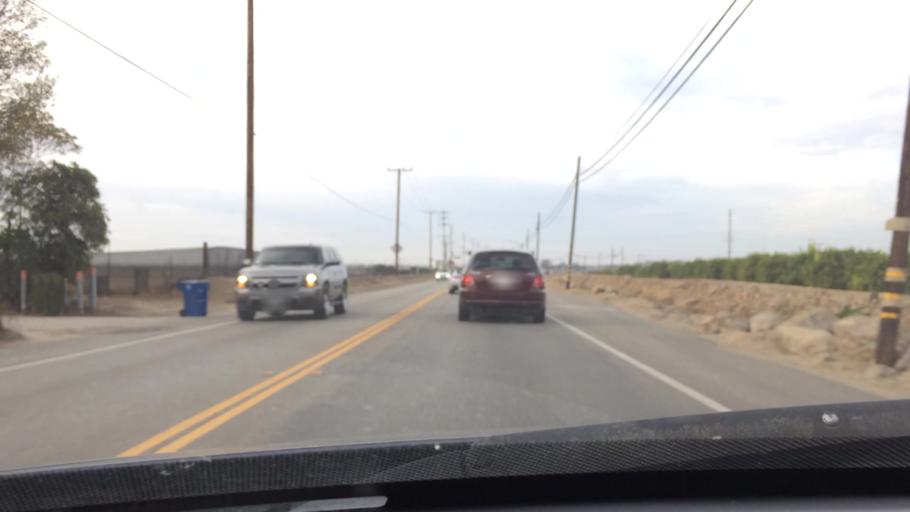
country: US
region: California
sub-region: Ventura County
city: Saticoy
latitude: 34.2578
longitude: -119.1071
